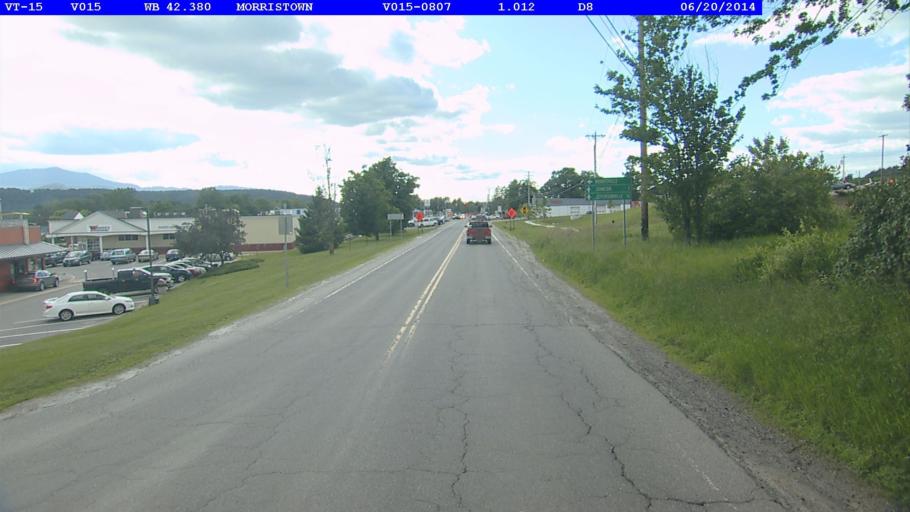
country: US
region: Vermont
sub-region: Lamoille County
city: Morrisville
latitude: 44.5743
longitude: -72.5903
